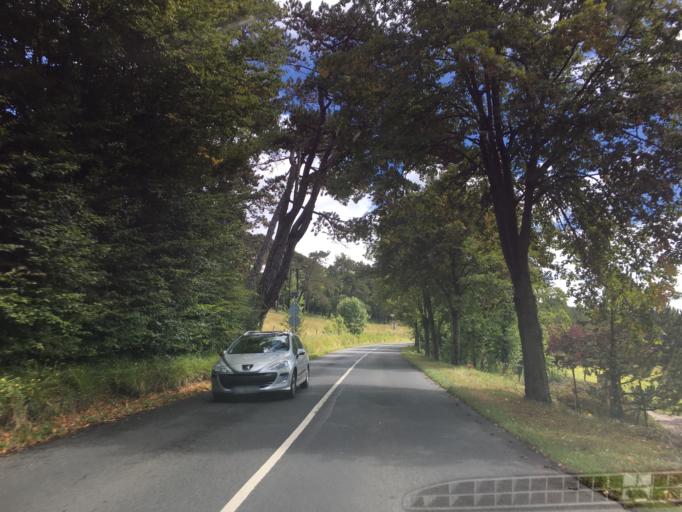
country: FR
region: Lower Normandy
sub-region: Departement du Calvados
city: Houlgate
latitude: 49.2872
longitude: -0.0857
